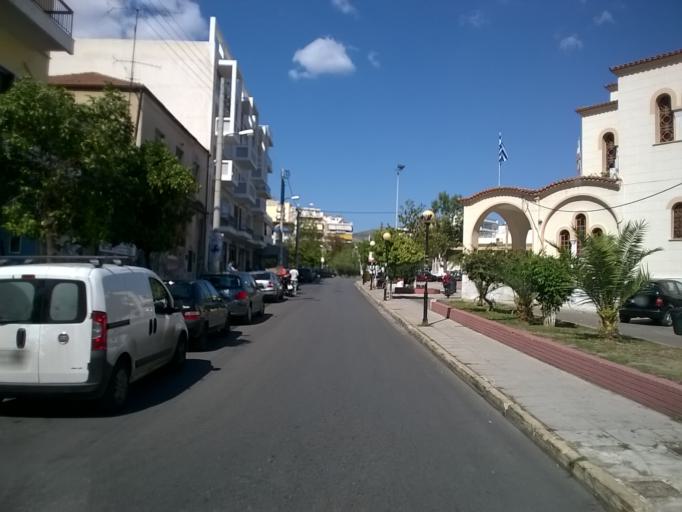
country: GR
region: Attica
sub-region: Nomos Piraios
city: Nikaia
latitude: 37.9698
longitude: 23.6539
